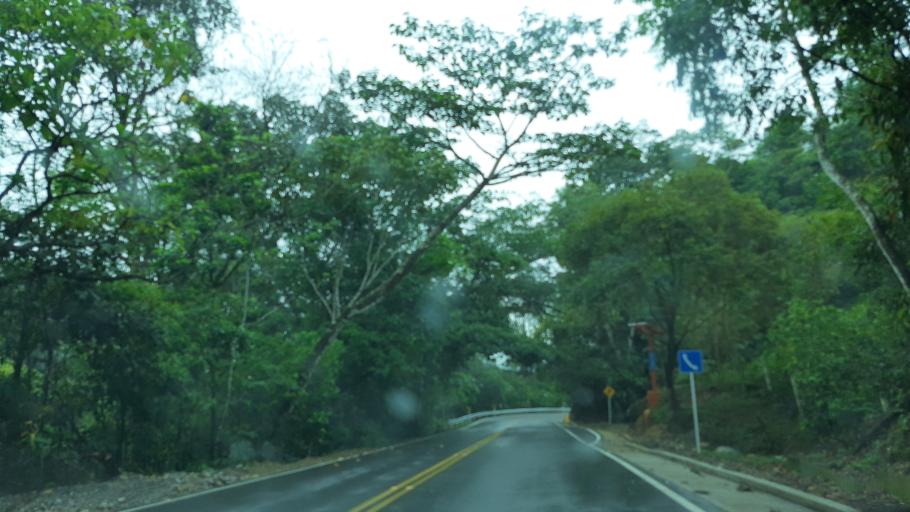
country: CO
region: Casanare
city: Sabanalarga
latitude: 4.7583
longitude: -73.0260
